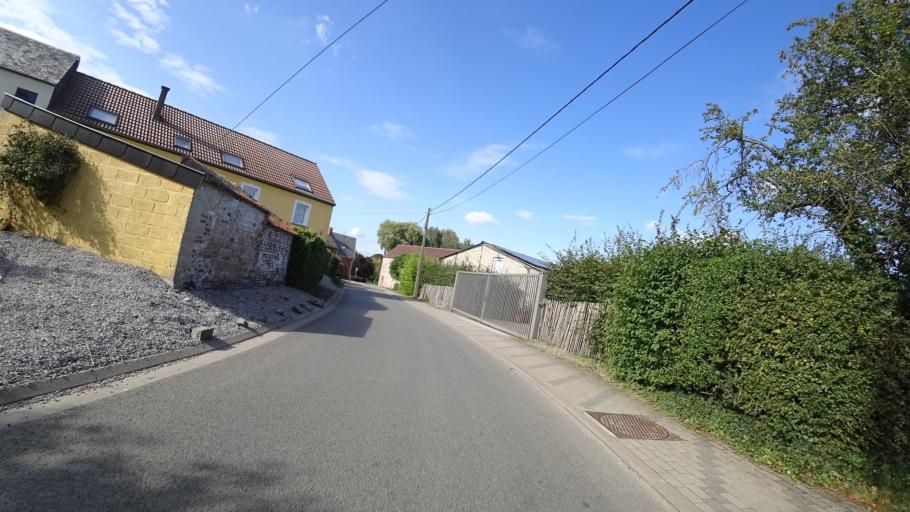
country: BE
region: Wallonia
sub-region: Province de Namur
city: Sombreffe
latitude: 50.5569
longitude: 4.6266
